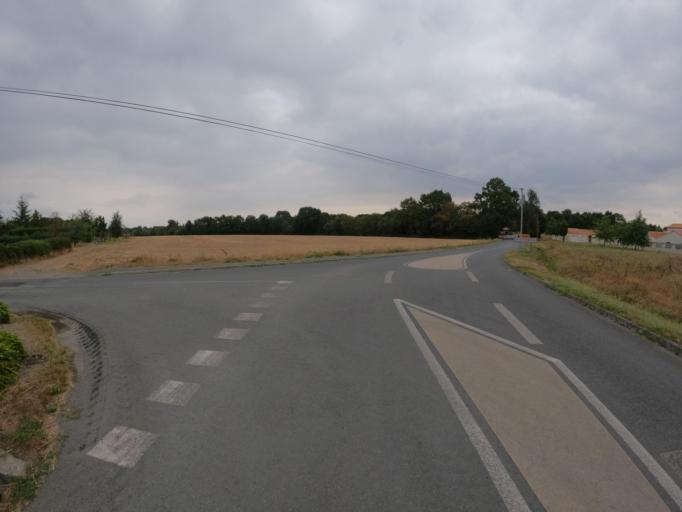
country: FR
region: Pays de la Loire
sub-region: Departement de la Vendee
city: La Guyonniere
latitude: 46.9690
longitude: -1.2574
